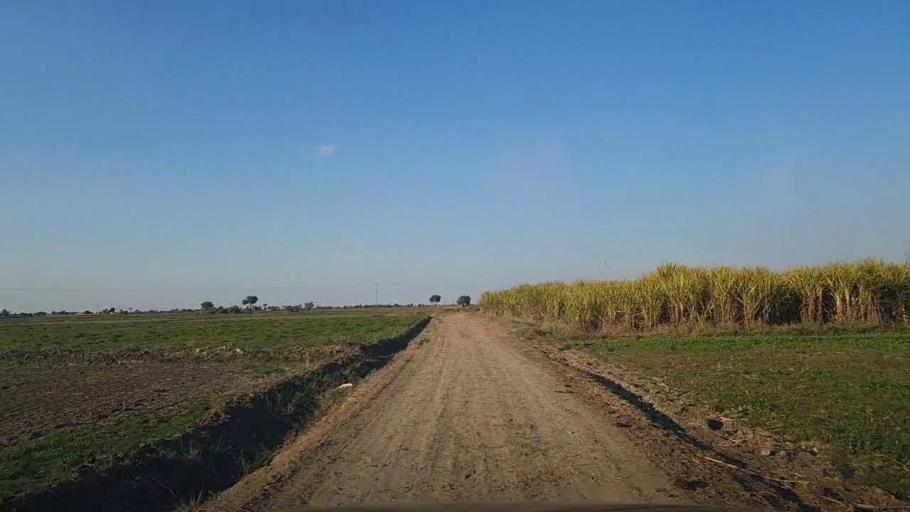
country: PK
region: Sindh
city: Sanghar
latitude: 25.9228
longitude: 69.0522
